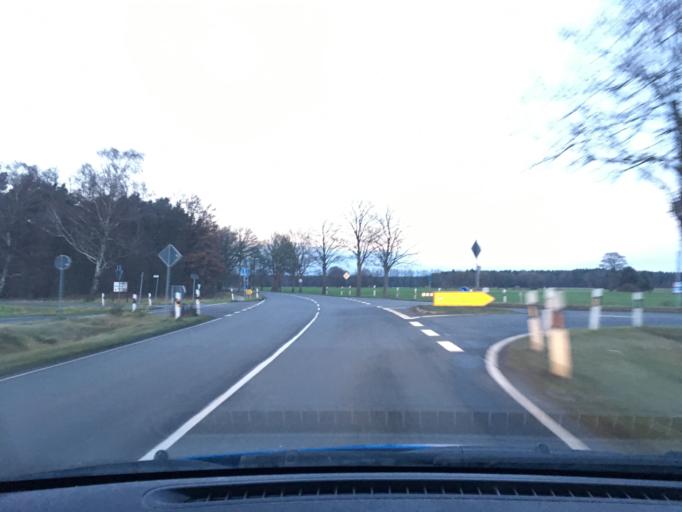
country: DE
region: Lower Saxony
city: Isernhagen Farster Bauerschaft
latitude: 52.5169
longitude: 9.8604
